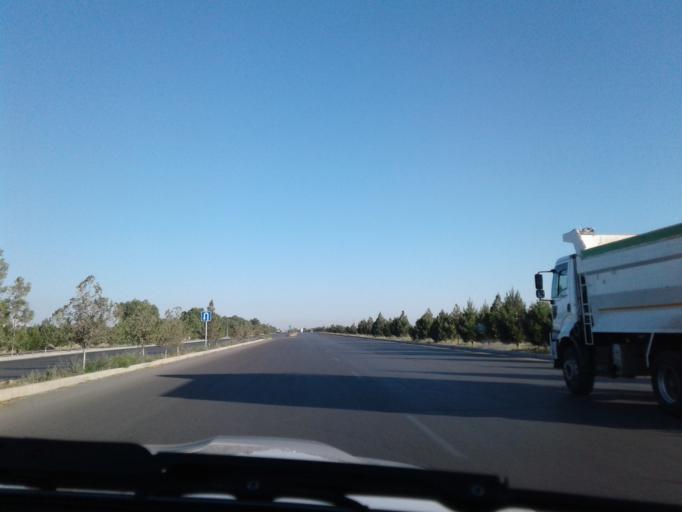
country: TM
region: Ahal
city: Abadan
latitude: 38.0658
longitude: 58.2542
